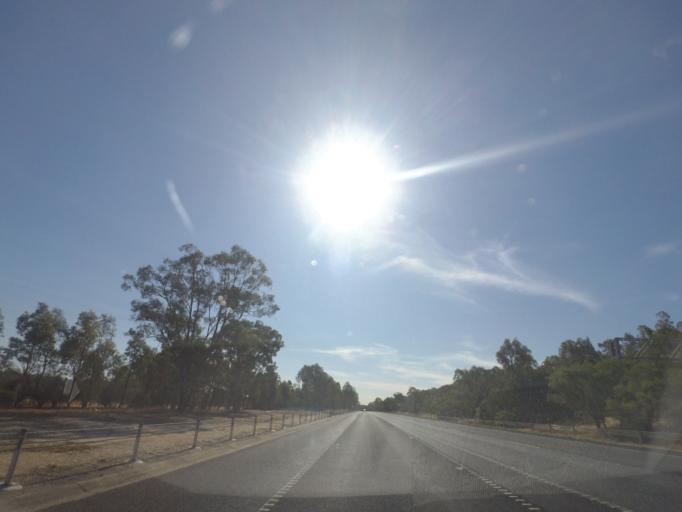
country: AU
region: Victoria
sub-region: Murrindindi
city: Kinglake West
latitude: -36.9837
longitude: 145.1371
